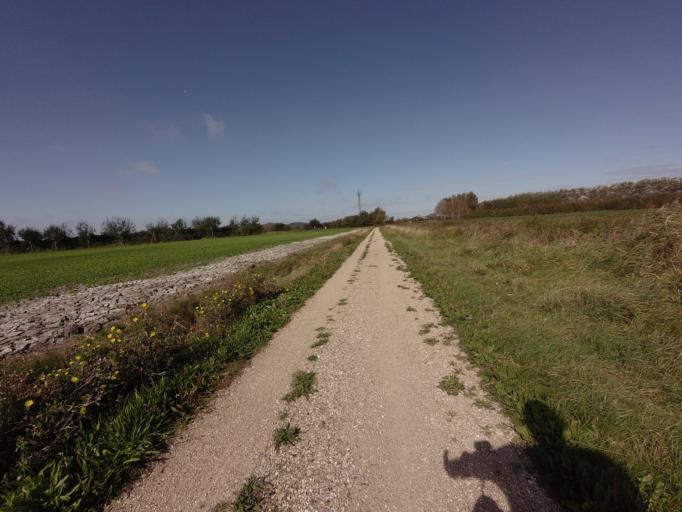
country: NL
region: Zeeland
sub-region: Gemeente Vlissingen
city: Vlissingen
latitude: 51.4859
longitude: 3.5313
